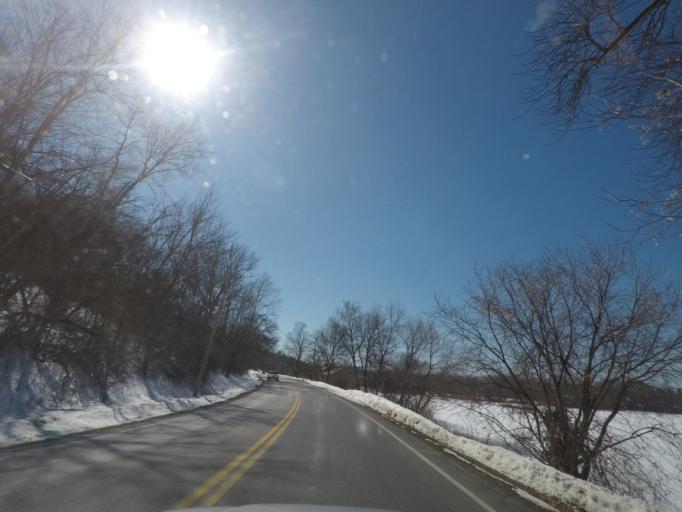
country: US
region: New York
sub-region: Saratoga County
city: Schuylerville
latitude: 43.0932
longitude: -73.5693
